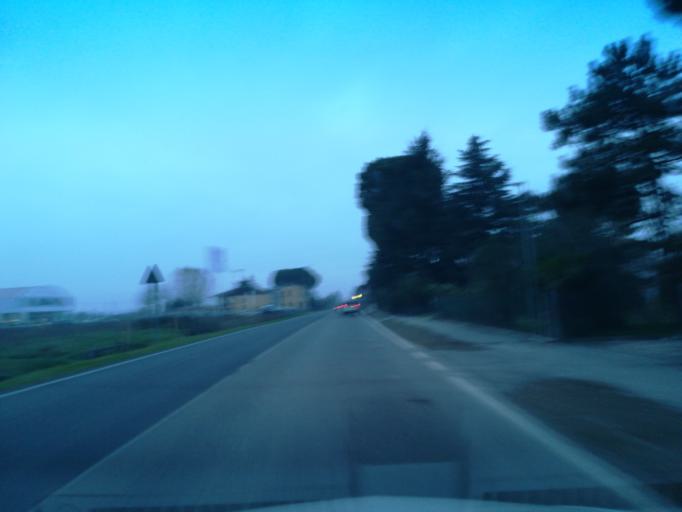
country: IT
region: Emilia-Romagna
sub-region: Provincia di Ravenna
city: Faenza
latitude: 44.3012
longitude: 11.8452
